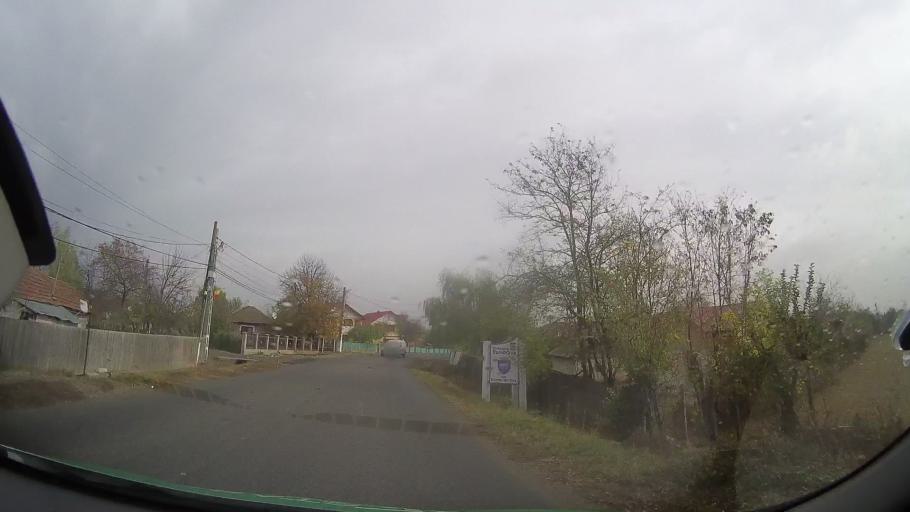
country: RO
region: Prahova
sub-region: Comuna Rafov
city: Palanca
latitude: 44.8413
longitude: 26.2408
